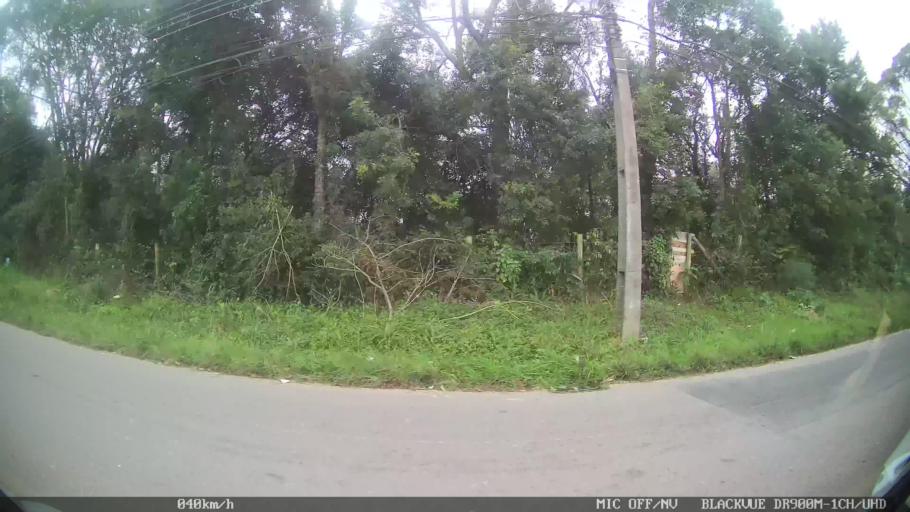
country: BR
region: Parana
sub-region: Almirante Tamandare
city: Almirante Tamandare
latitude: -25.3567
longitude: -49.2724
